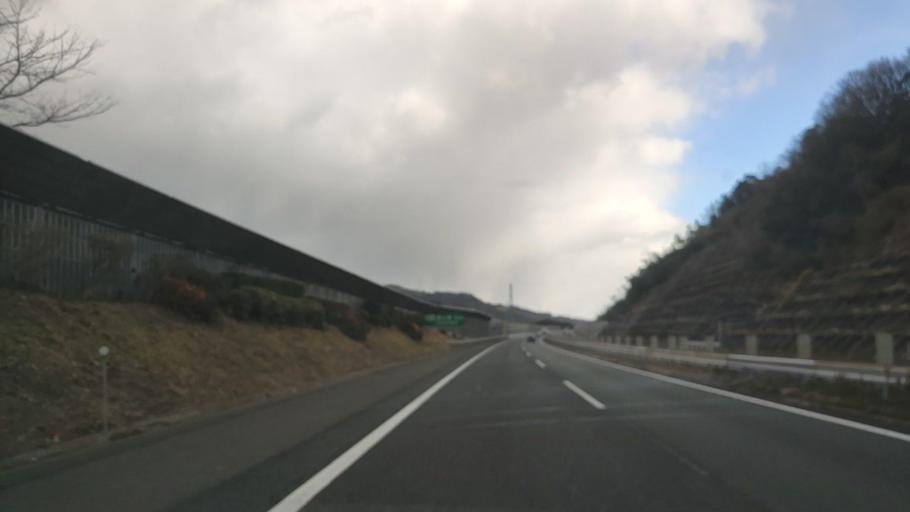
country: JP
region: Hiroshima
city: Fukuyama
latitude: 34.5168
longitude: 133.3712
